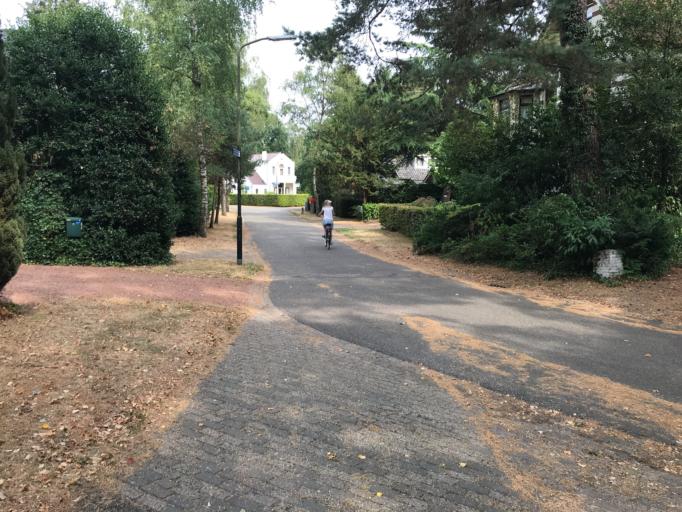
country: NL
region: Gelderland
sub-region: Gemeente Apeldoorn
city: Apeldoorn
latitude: 52.2258
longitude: 5.9350
